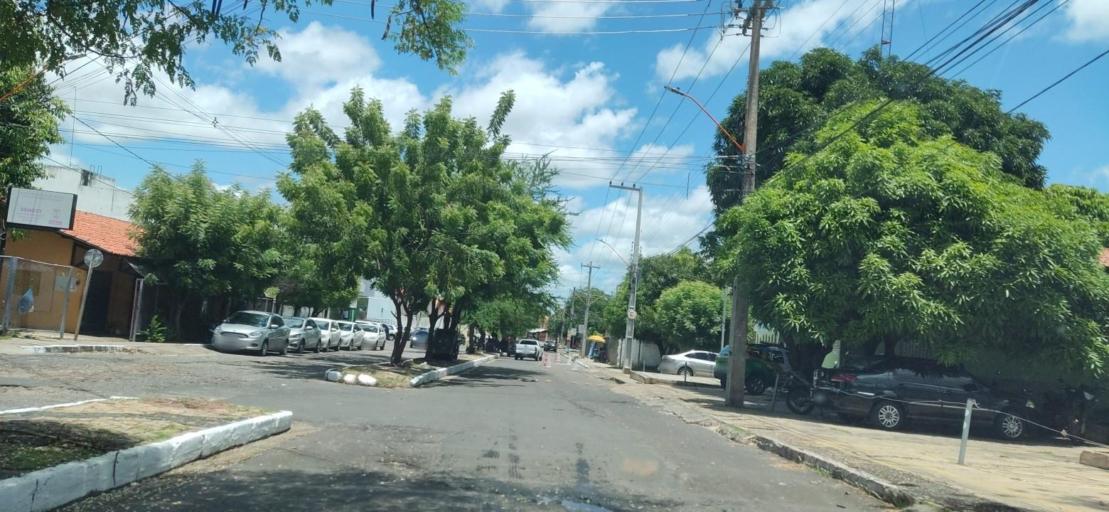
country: BR
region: Piaui
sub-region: Teresina
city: Teresina
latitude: -5.1473
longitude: -42.7823
